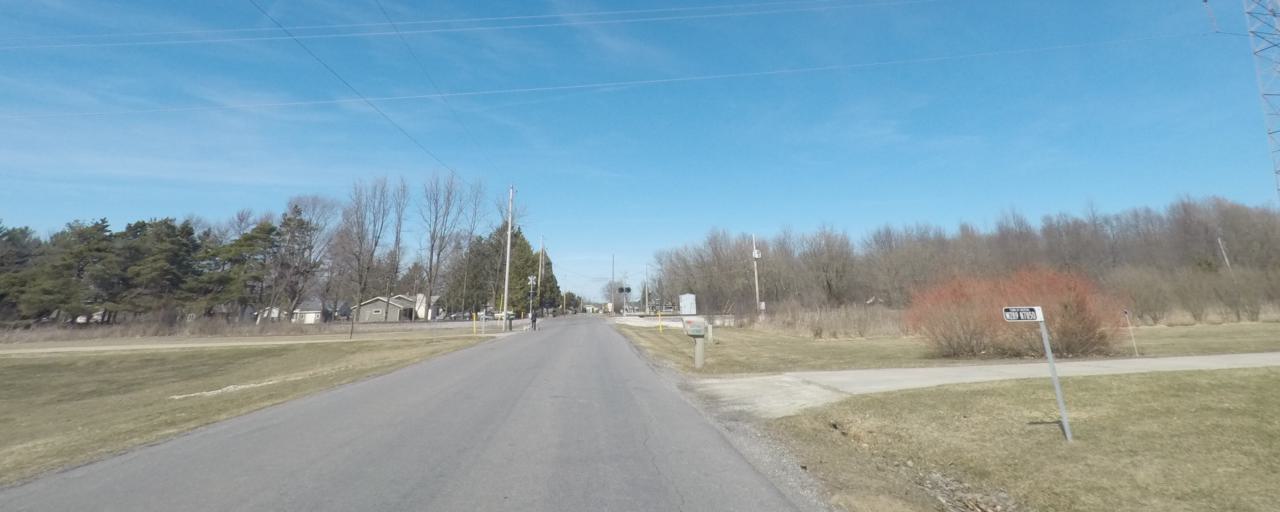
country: US
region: Wisconsin
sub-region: Waukesha County
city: Merton
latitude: 43.1590
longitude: -88.3214
